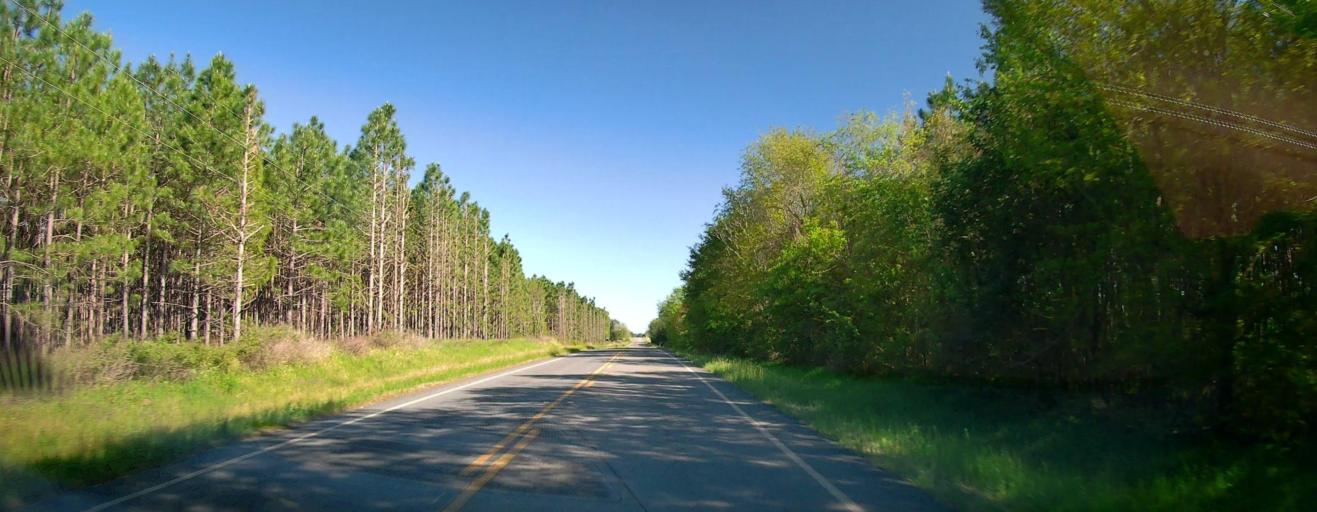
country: US
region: Georgia
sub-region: Wilcox County
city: Rochelle
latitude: 31.9970
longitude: -83.4752
